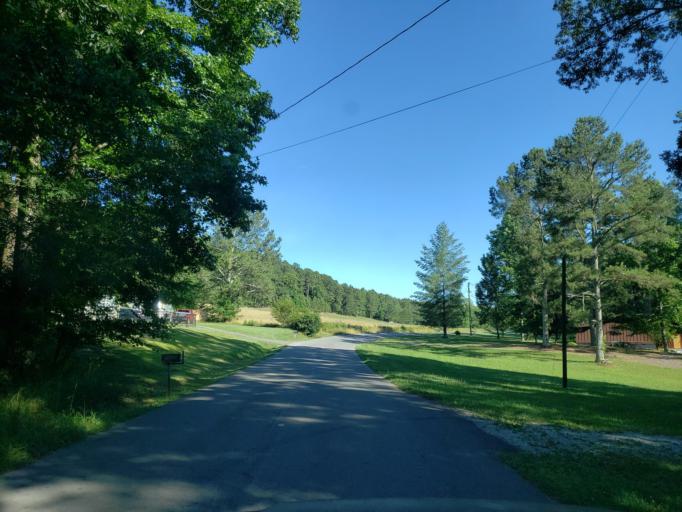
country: US
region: Georgia
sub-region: Whitfield County
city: Dalton
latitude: 34.6604
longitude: -85.0928
